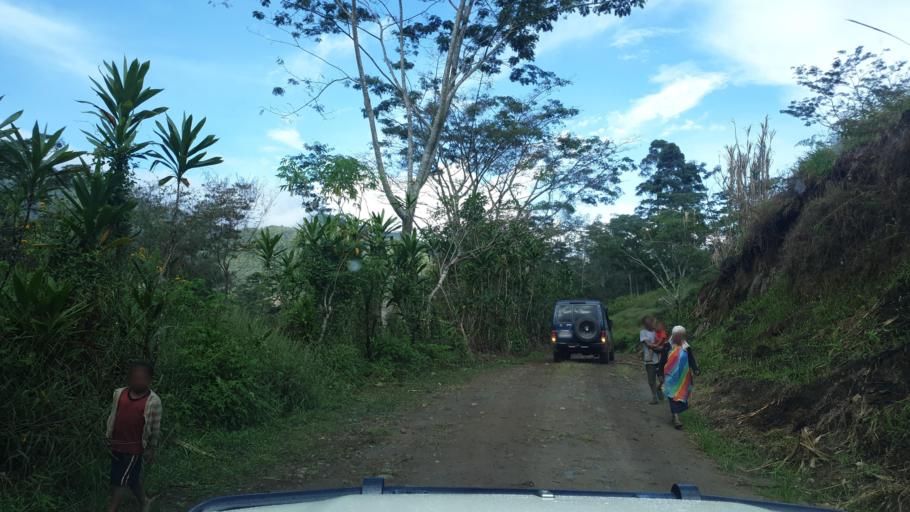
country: PG
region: Eastern Highlands
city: Goroka
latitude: -5.9201
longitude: 145.2573
